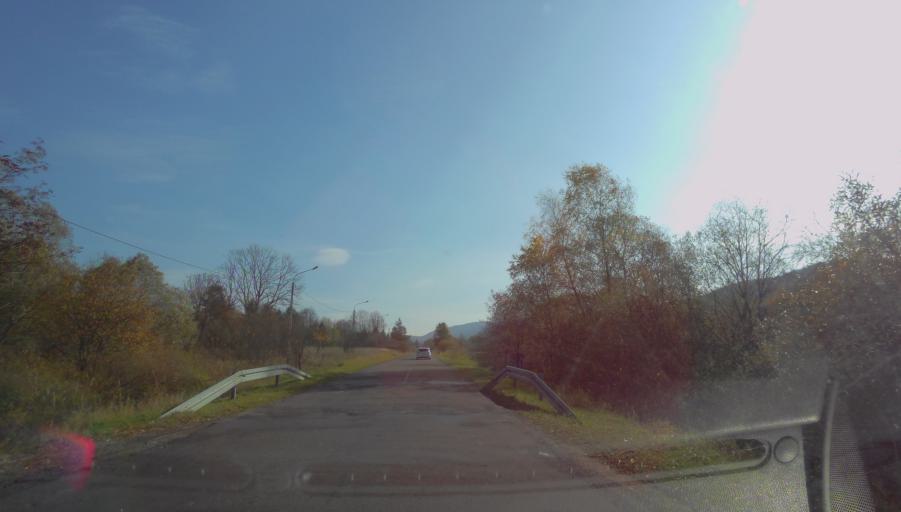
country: PL
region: Subcarpathian Voivodeship
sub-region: Powiat sanocki
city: Komancza
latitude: 49.2303
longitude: 22.1626
